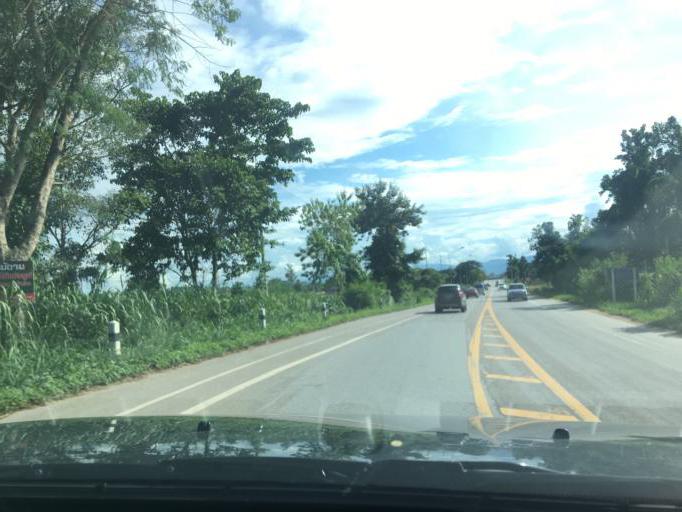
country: TH
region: Chiang Rai
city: Mae Suai
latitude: 19.6614
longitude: 99.5485
